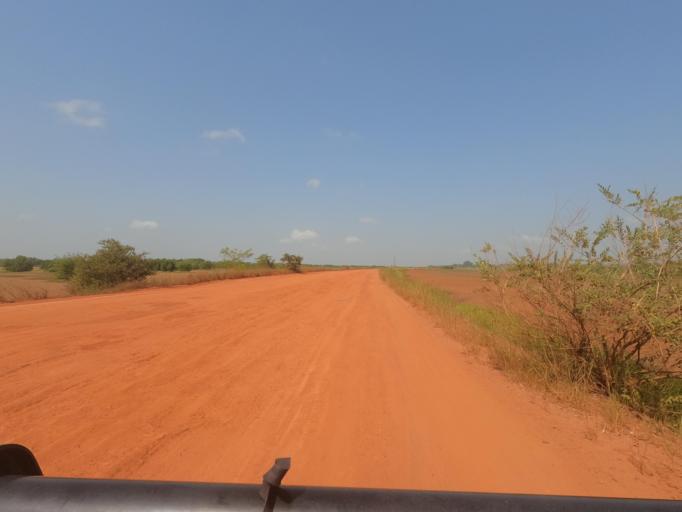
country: GW
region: Cacheu
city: Canchungo
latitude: 12.2553
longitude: -15.7777
